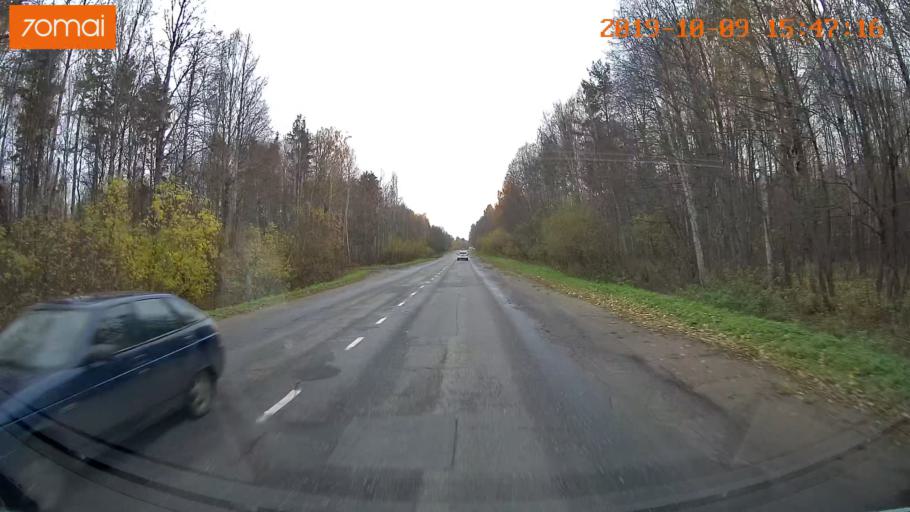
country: RU
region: Kostroma
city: Oktyabr'skiy
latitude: 57.8187
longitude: 41.0311
